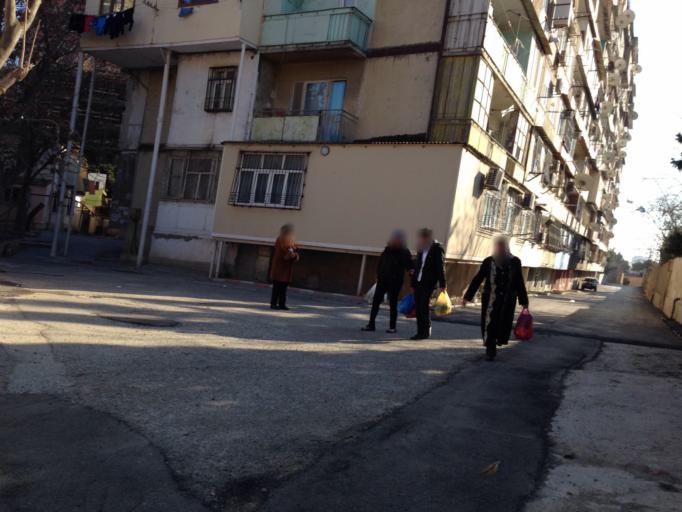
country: AZ
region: Baki
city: Baku
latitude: 40.3917
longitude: 49.8768
